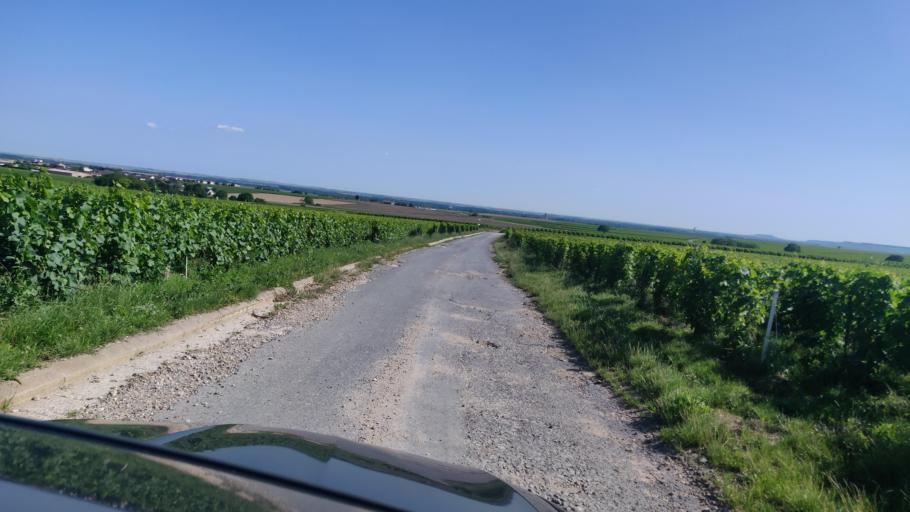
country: FR
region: Champagne-Ardenne
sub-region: Departement de la Marne
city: Tours-sur-Marne
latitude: 49.0877
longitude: 4.1352
